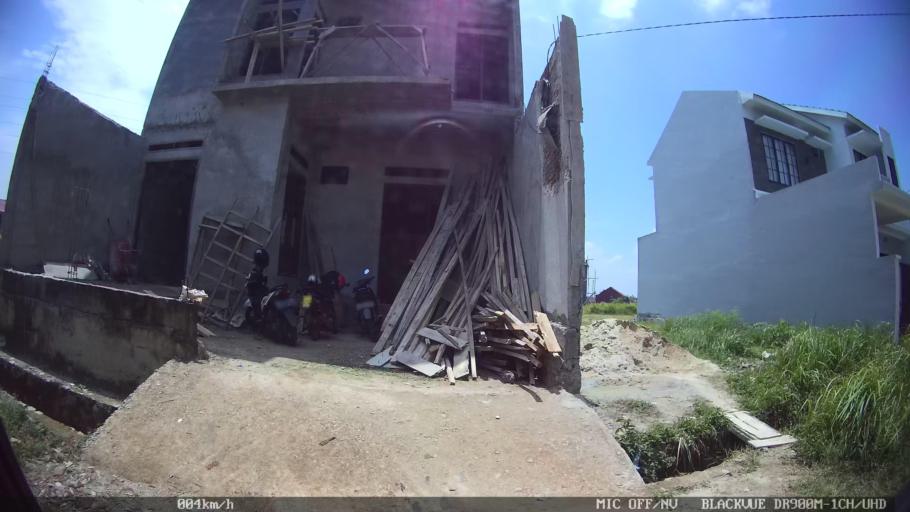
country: ID
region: Lampung
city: Kedaton
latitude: -5.3559
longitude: 105.2901
